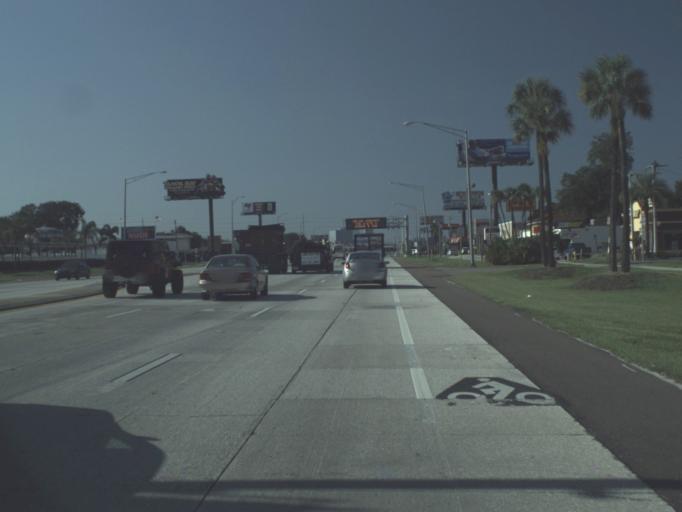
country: US
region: Florida
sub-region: Hillsborough County
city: Tampa
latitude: 27.9639
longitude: -82.5057
